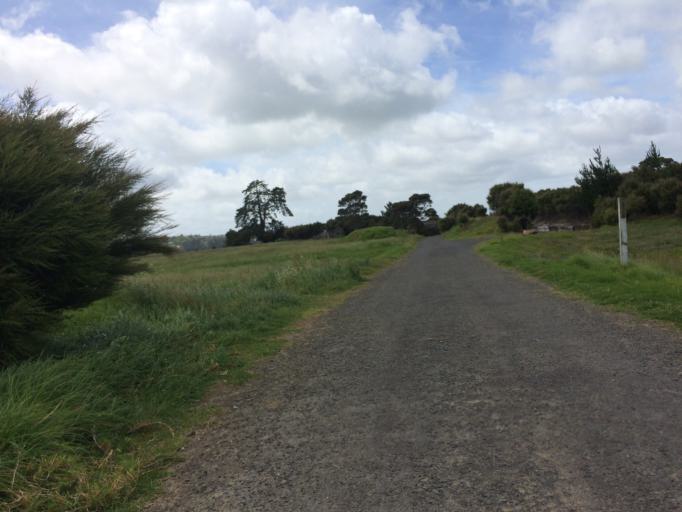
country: NZ
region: Auckland
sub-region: Auckland
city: North Shore
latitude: -36.7957
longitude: 174.6712
